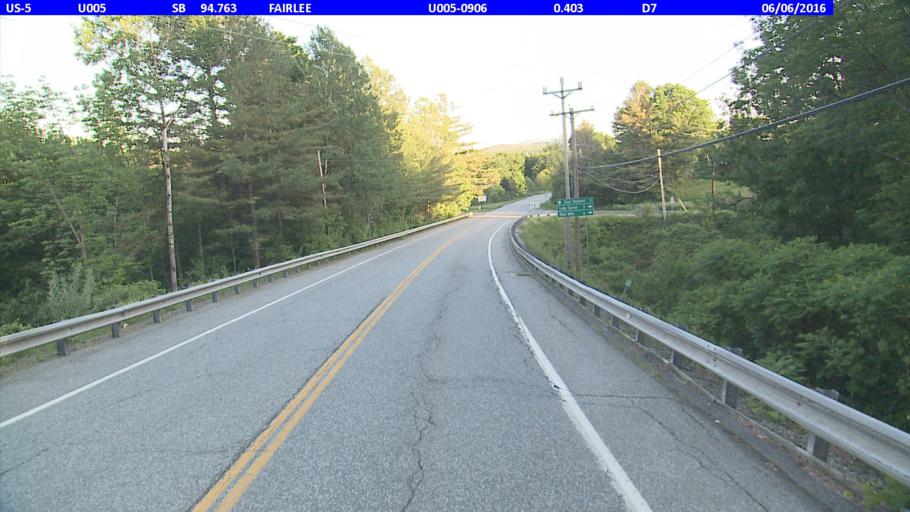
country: US
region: New Hampshire
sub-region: Grafton County
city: Orford
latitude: 43.8796
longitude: -72.1767
